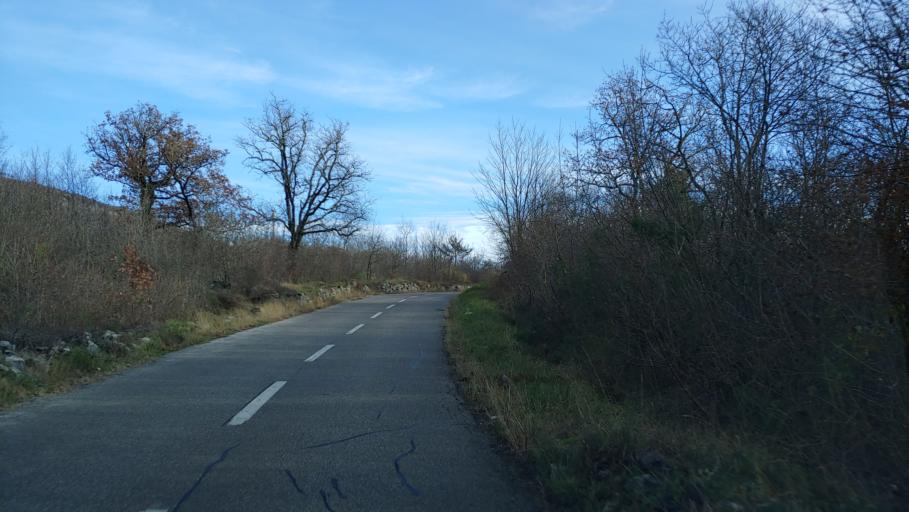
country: IT
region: Friuli Venezia Giulia
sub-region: Provincia di Trieste
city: Duino
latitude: 45.8122
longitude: 13.6158
